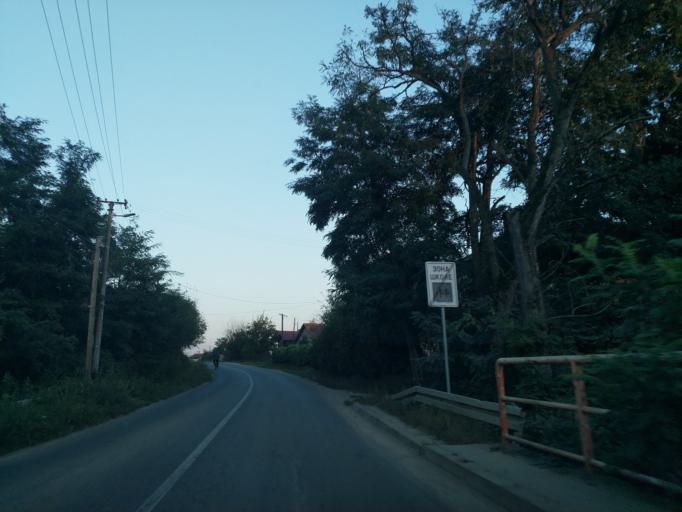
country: RS
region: Central Serbia
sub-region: Rasinski Okrug
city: Krusevac
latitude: 43.6051
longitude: 21.2405
